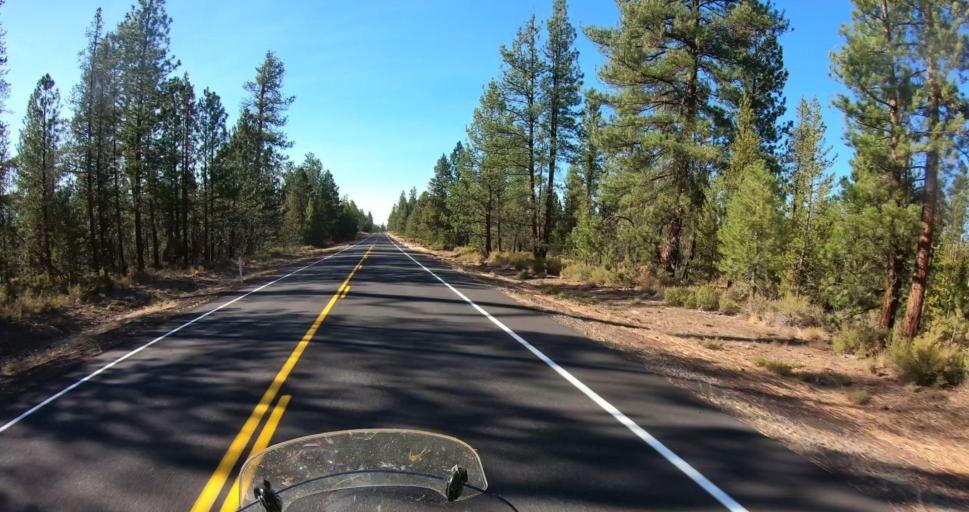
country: US
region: Oregon
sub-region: Deschutes County
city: La Pine
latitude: 43.4880
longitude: -121.4327
